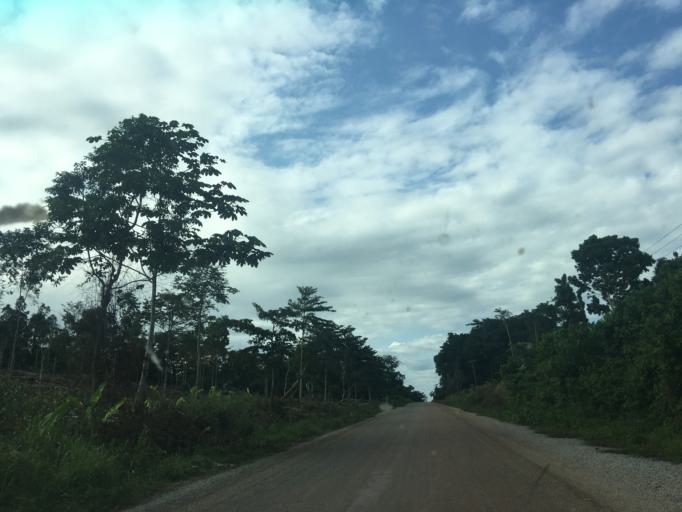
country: GH
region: Western
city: Wassa-Akropong
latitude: 5.9896
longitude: -2.4119
